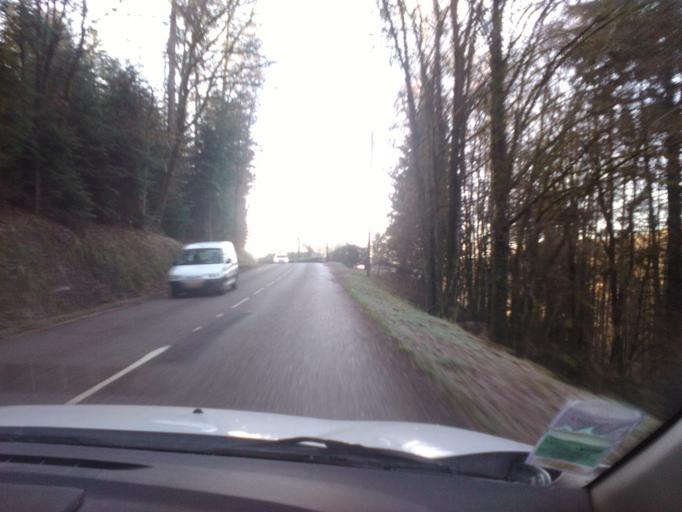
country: FR
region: Lorraine
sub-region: Departement des Vosges
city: Plombieres-les-Bains
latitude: 47.9575
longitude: 6.4537
